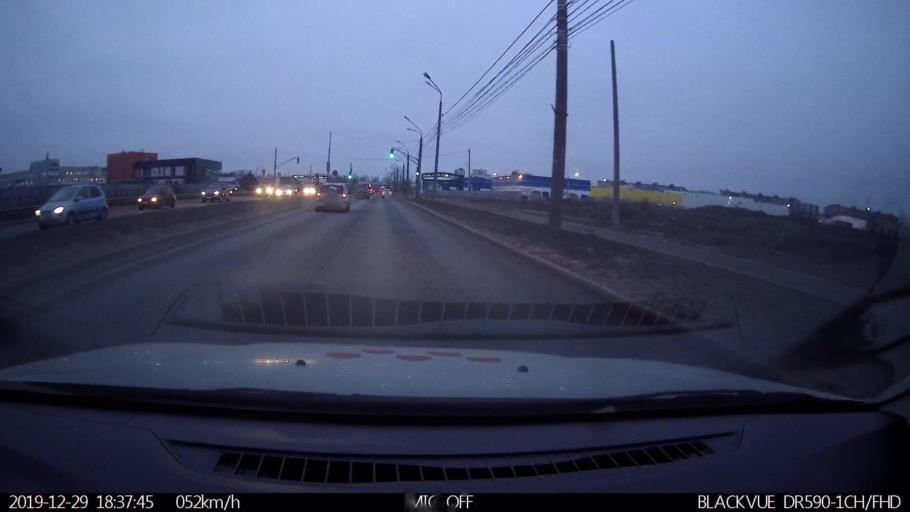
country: RU
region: Nizjnij Novgorod
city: Neklyudovo
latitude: 56.3426
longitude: 43.8887
